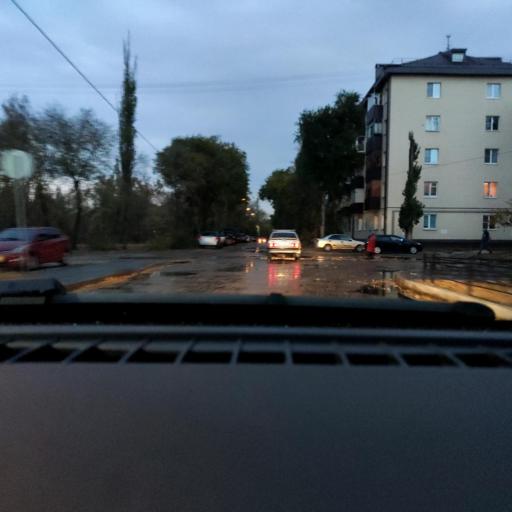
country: RU
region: Voronezj
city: Maslovka
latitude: 51.6181
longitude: 39.2419
